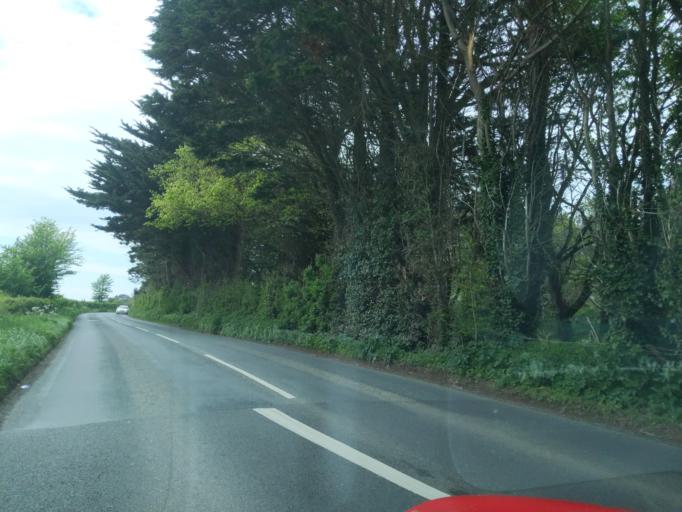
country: GB
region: England
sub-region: Cornwall
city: Wadebridge
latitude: 50.5341
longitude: -4.8427
